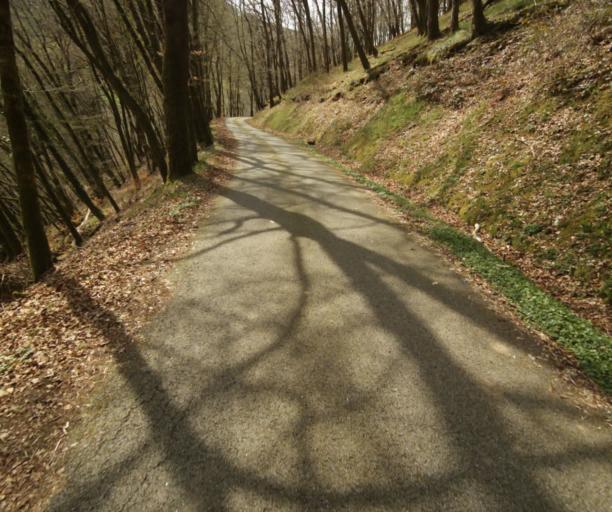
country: FR
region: Limousin
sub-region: Departement de la Correze
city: Naves
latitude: 45.3425
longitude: 1.8017
